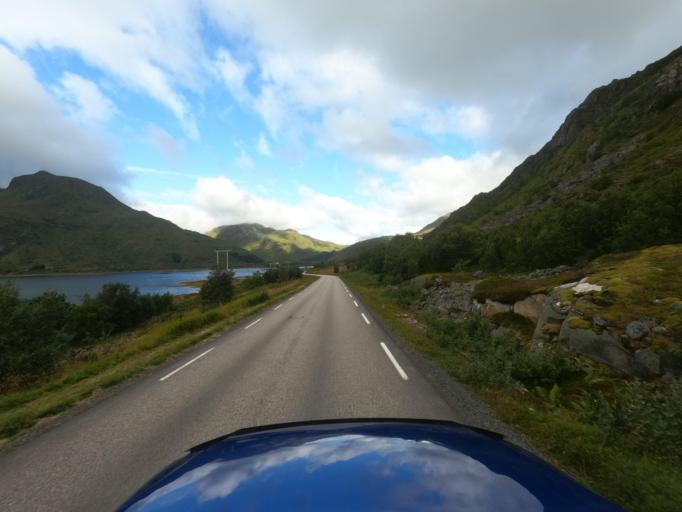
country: NO
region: Nordland
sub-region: Vestvagoy
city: Evjen
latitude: 68.1858
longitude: 13.8931
